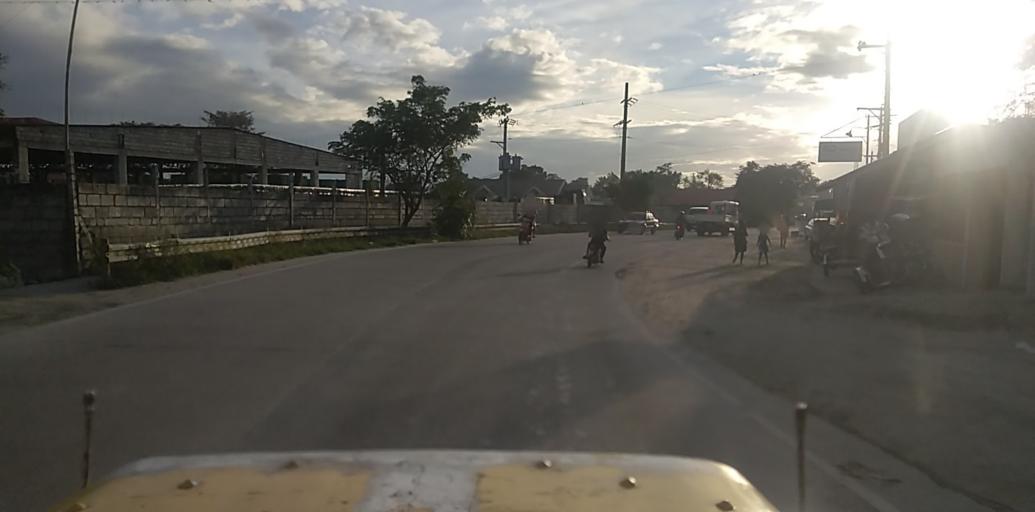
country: PH
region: Central Luzon
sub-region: Province of Pampanga
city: Malino
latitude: 15.1291
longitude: 120.6760
